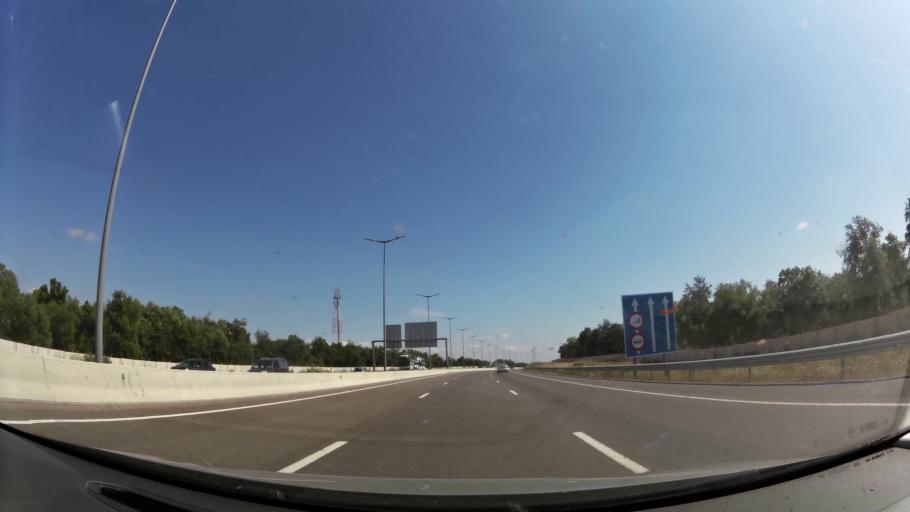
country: MA
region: Rabat-Sale-Zemmour-Zaer
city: Sale
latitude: 34.0175
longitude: -6.7084
